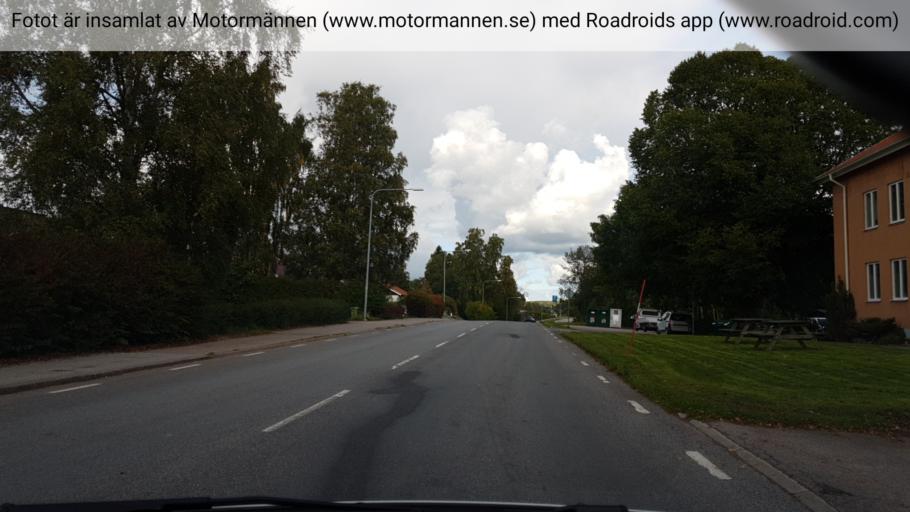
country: SE
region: Vaestra Goetaland
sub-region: Tibro Kommun
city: Tibro
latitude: 58.4143
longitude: 14.1804
